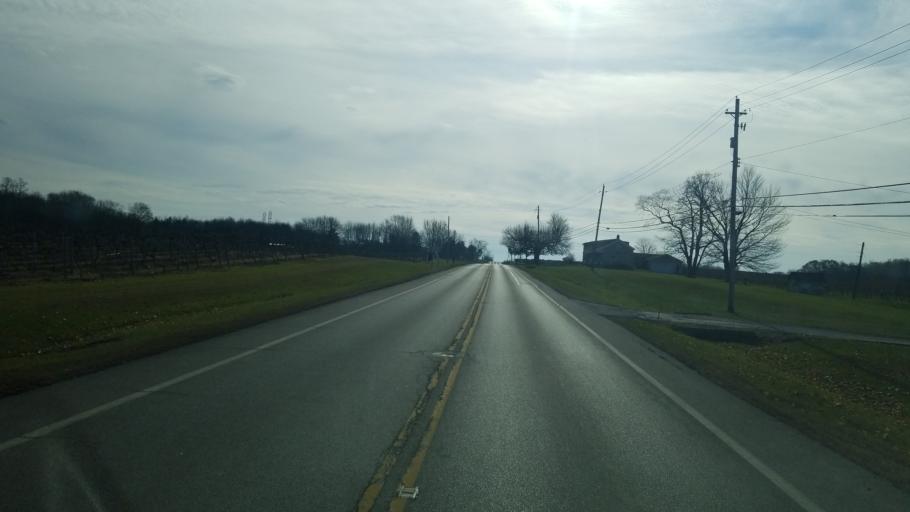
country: US
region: Ohio
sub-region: Ashtabula County
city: Geneva
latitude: 41.7407
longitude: -80.9524
